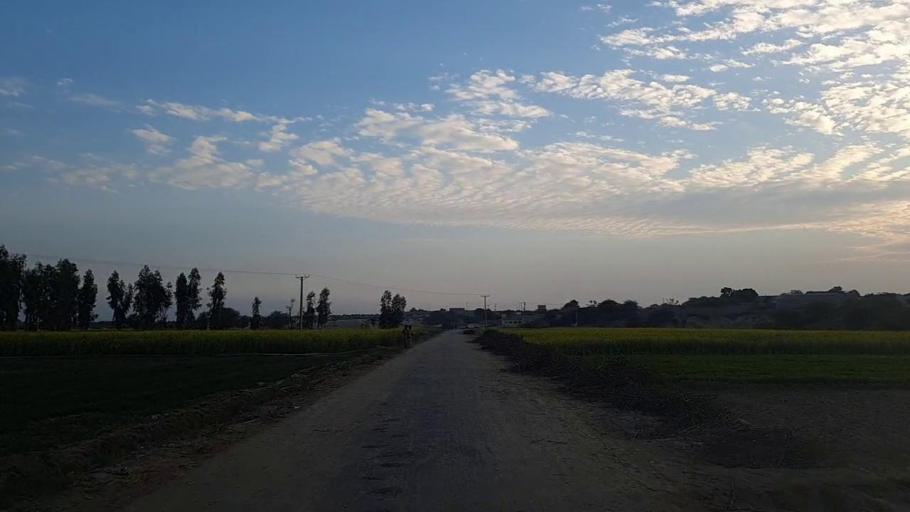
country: PK
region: Sindh
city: Daur
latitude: 26.4149
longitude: 68.4678
